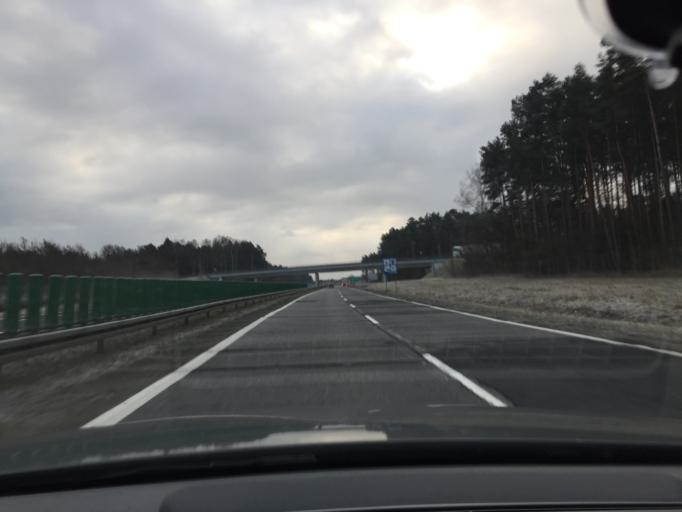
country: PL
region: Lubusz
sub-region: Powiat zarski
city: Trzebiel
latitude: 51.6367
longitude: 14.8711
